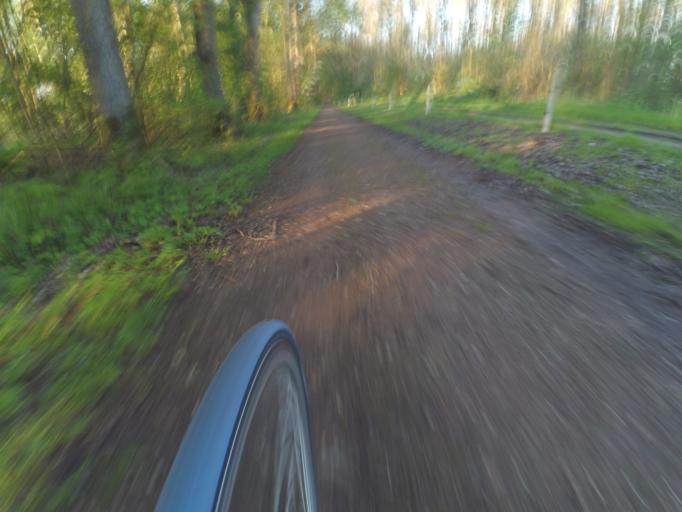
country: NL
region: Flevoland
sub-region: Gemeente Lelystad
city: Lelystad
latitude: 52.4209
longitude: 5.4918
